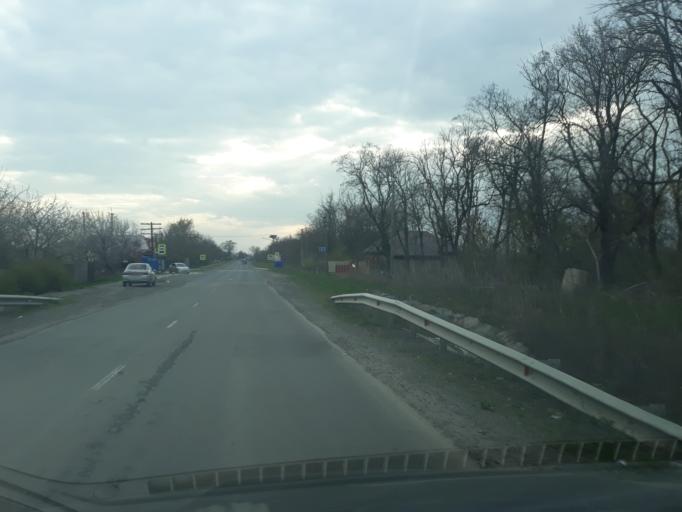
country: RU
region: Rostov
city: Novobessergenovka
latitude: 47.1785
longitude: 38.7886
